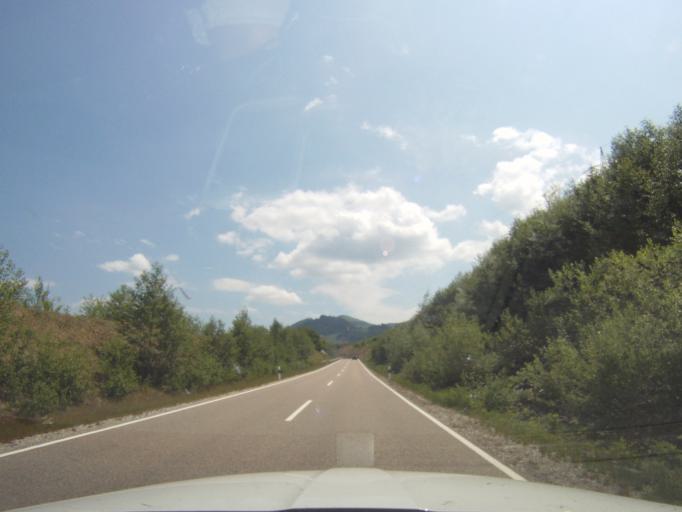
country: DE
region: Bavaria
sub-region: Swabia
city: Wertach
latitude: 47.5975
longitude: 10.4090
